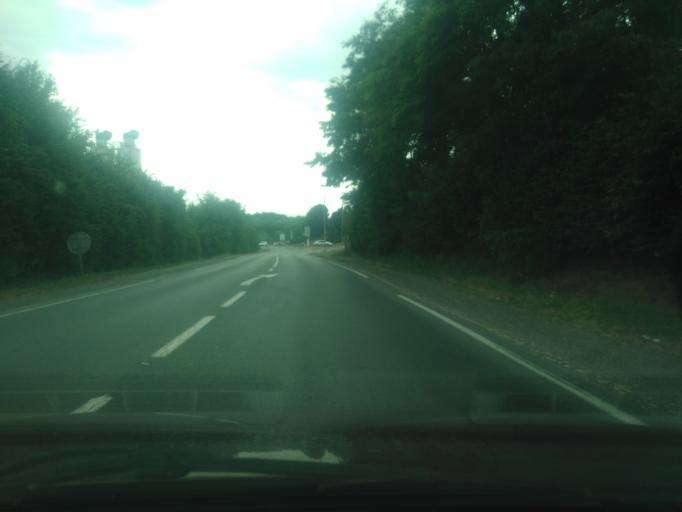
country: FR
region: Pays de la Loire
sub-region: Departement de la Vendee
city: Chantonnay
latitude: 46.6974
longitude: -1.0552
